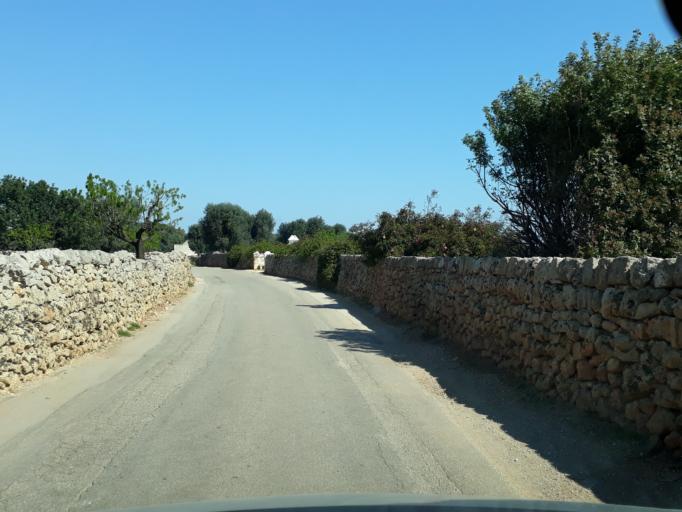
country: IT
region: Apulia
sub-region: Provincia di Brindisi
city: Fasano
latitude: 40.8332
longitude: 17.3784
